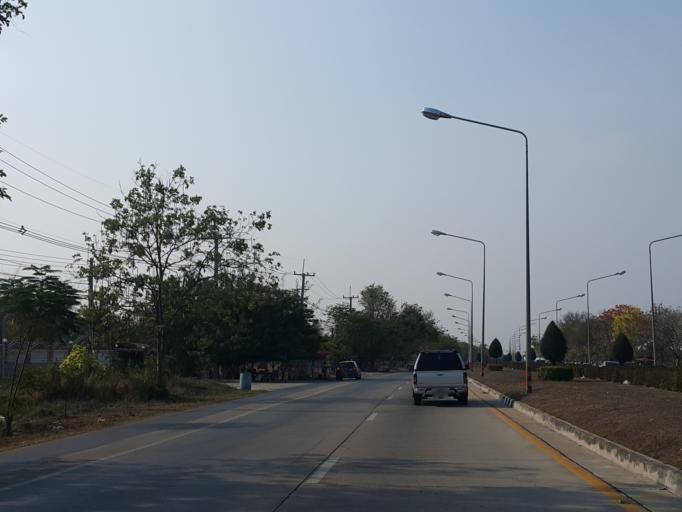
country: TH
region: Suphan Buri
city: Sam Chuk
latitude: 14.7641
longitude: 100.0937
